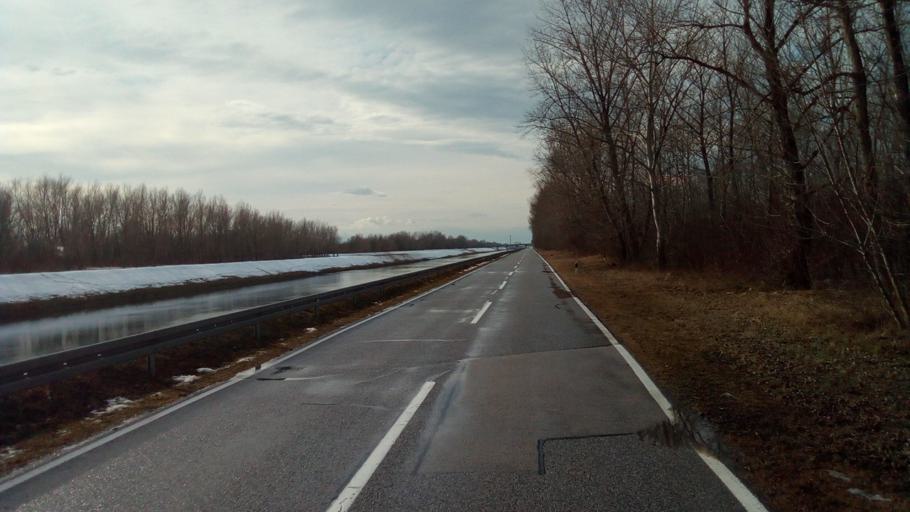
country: HR
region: Medimurska
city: Orehovica
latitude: 46.3174
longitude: 16.5359
